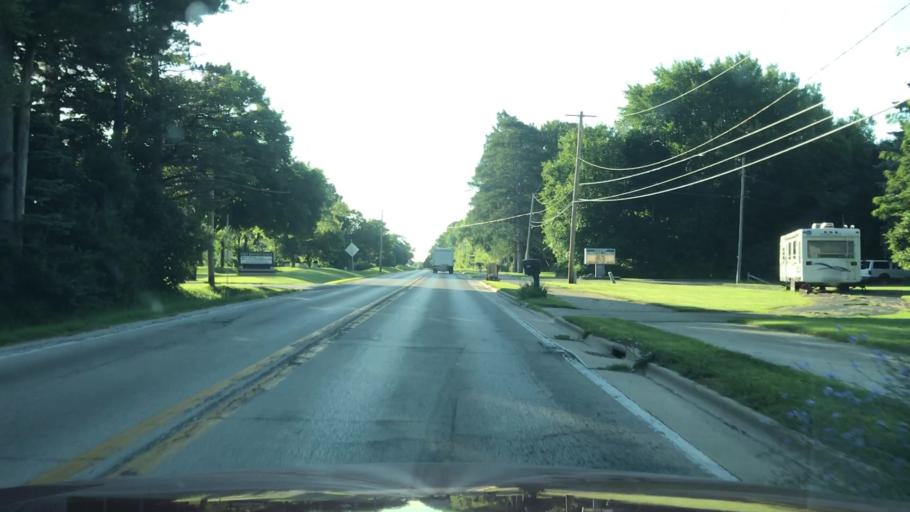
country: US
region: Illinois
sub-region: Winnebago County
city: Cherry Valley
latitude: 42.2459
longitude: -89.0111
